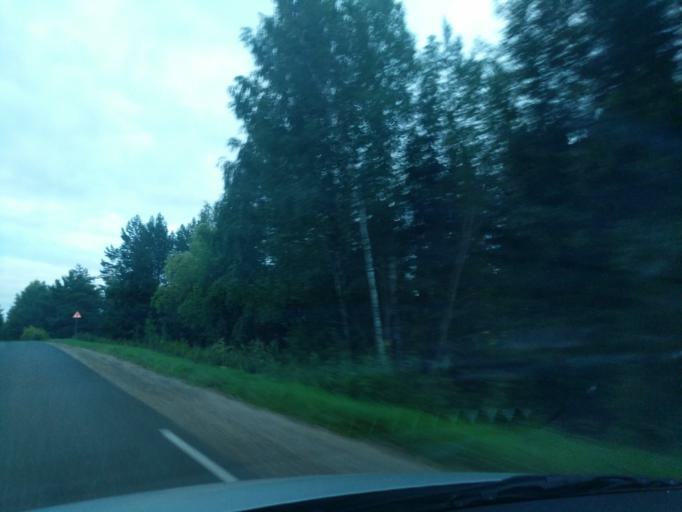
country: RU
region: Kirov
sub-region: Kirovo-Chepetskiy Rayon
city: Kirov
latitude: 58.6046
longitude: 49.8144
